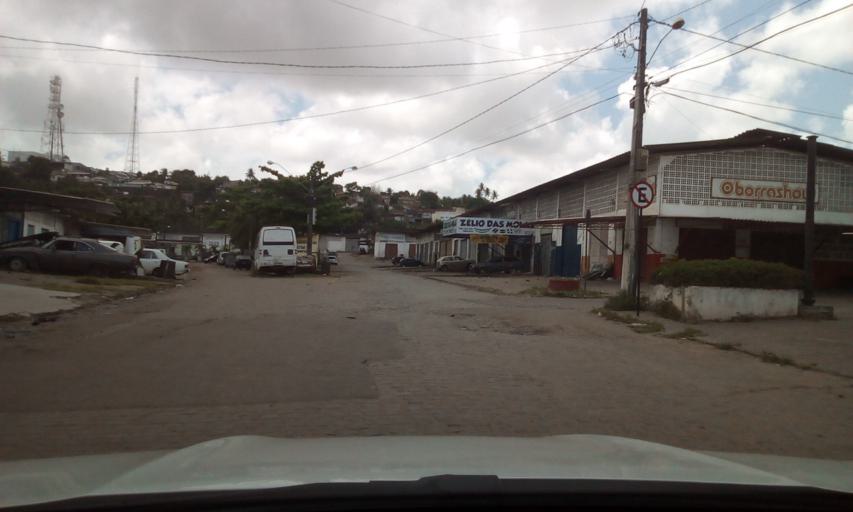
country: BR
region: Paraiba
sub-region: Joao Pessoa
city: Joao Pessoa
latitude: -7.1287
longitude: -34.8893
